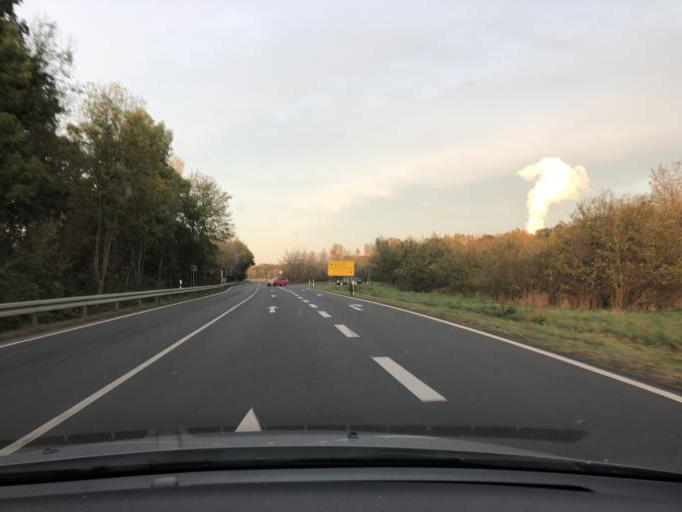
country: DE
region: Saxony
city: Groitzsch
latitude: 51.1680
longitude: 12.2727
